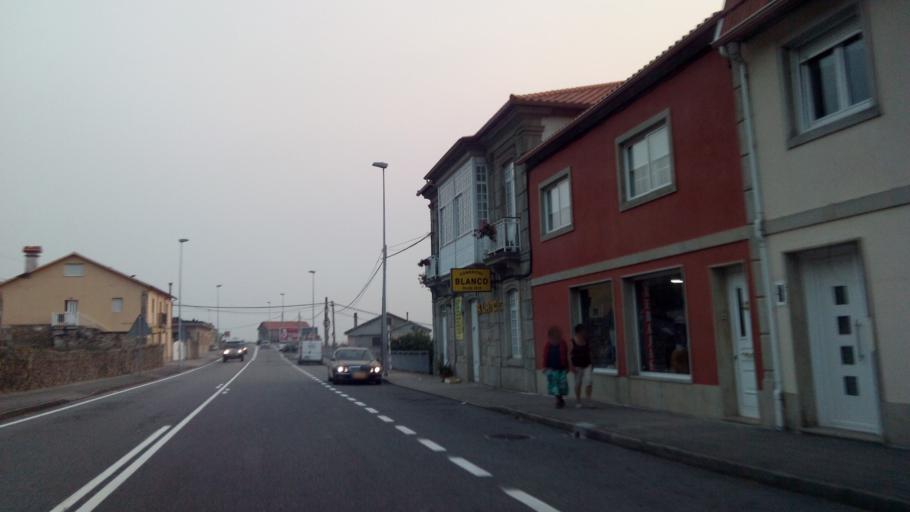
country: ES
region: Galicia
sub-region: Provincia de Pontevedra
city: Oia
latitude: 42.0014
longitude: -8.8742
